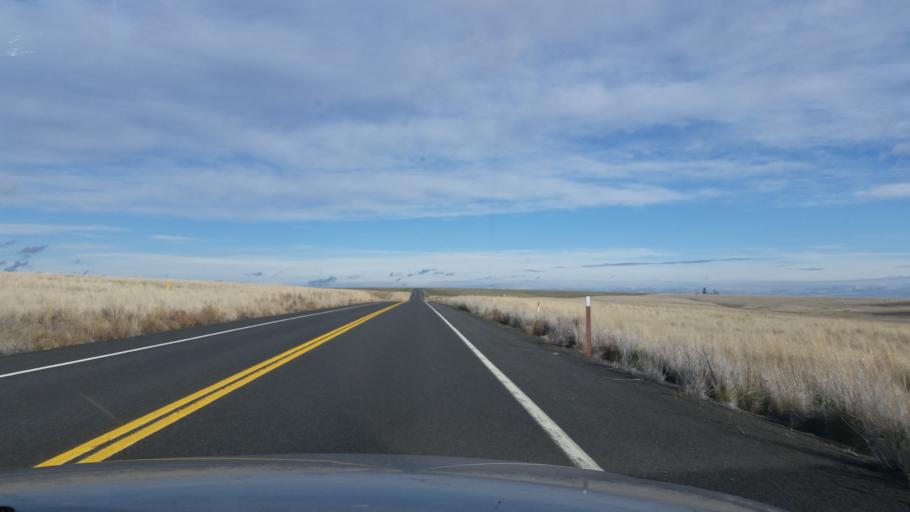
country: US
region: Washington
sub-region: Adams County
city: Ritzville
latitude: 47.3732
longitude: -118.4445
